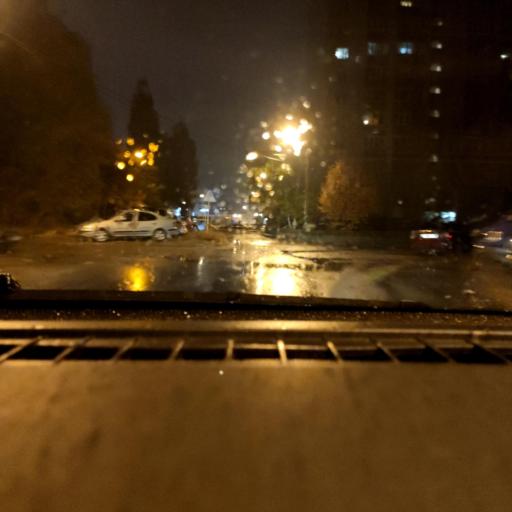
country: RU
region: Voronezj
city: Podgornoye
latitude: 51.7193
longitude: 39.1710
